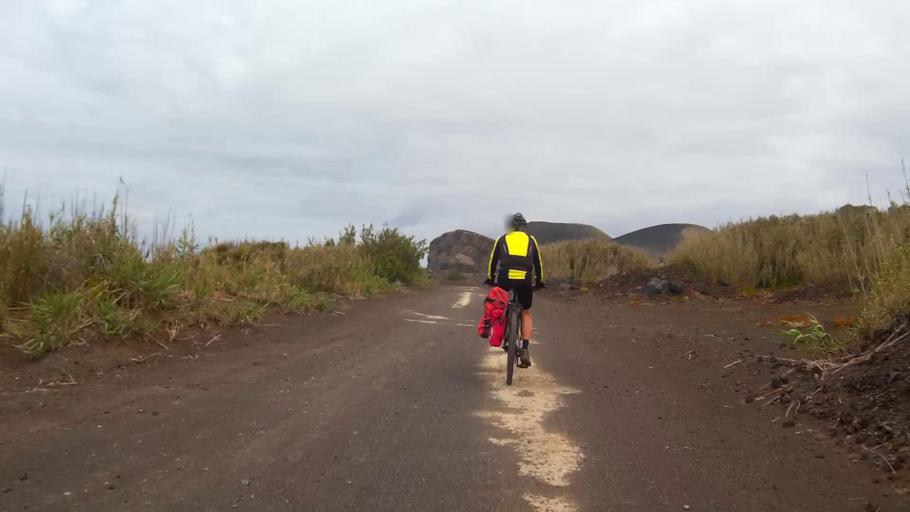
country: PT
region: Azores
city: Ribeira Grande
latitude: 38.5916
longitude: -28.8243
